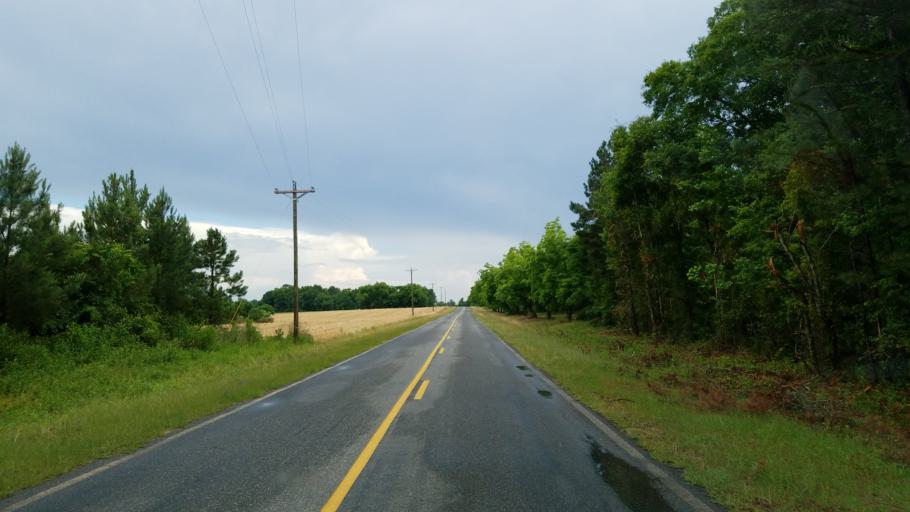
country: US
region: Georgia
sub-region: Dooly County
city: Unadilla
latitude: 32.2037
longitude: -83.7982
